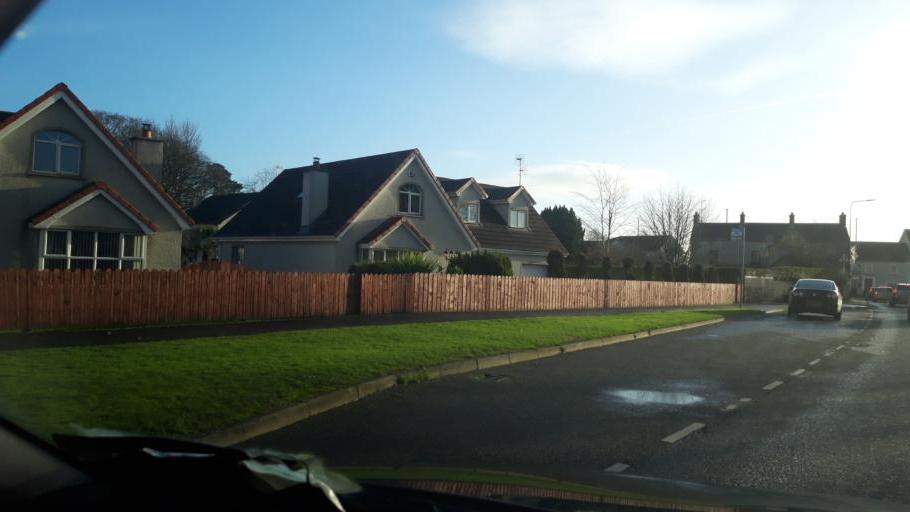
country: GB
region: Northern Ireland
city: Maghera
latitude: 54.8126
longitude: -6.7062
